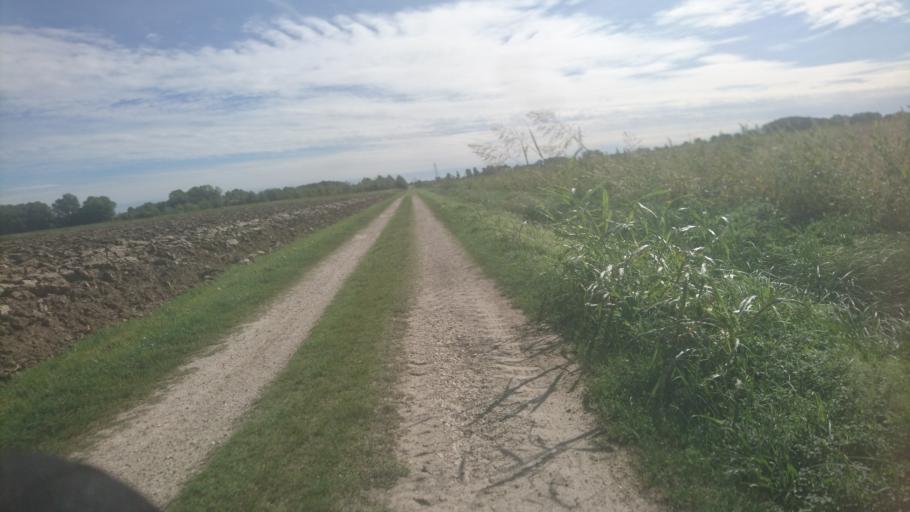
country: IT
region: Veneto
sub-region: Provincia di Padova
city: Veggiano
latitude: 45.4350
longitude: 11.7158
